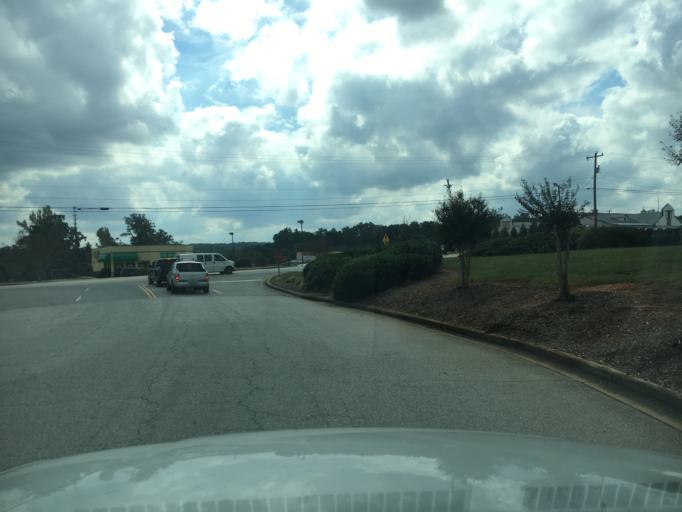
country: US
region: South Carolina
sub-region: Spartanburg County
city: Landrum
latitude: 35.1826
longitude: -82.1602
